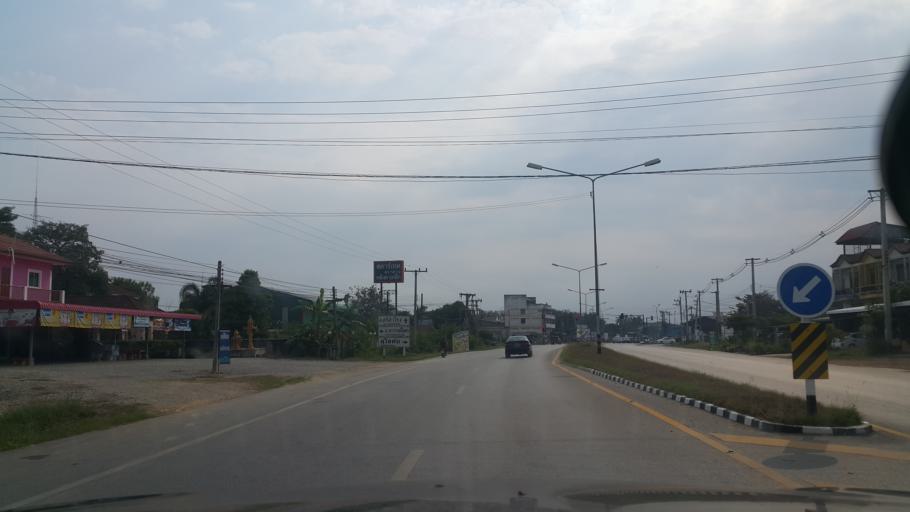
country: TH
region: Sukhothai
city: Si Samrong
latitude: 17.1761
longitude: 99.8502
